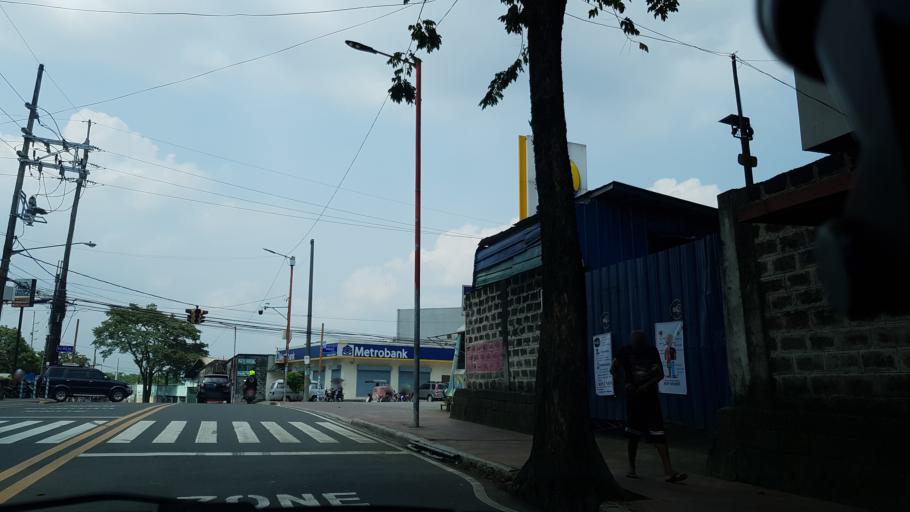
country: PH
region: Calabarzon
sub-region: Province of Rizal
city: Antipolo
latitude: 14.6597
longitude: 121.1187
